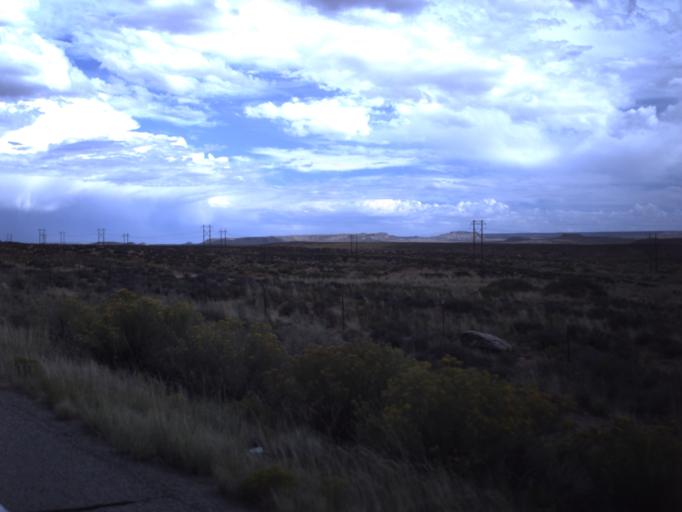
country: US
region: Utah
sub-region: San Juan County
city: Blanding
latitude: 37.3014
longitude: -109.4433
